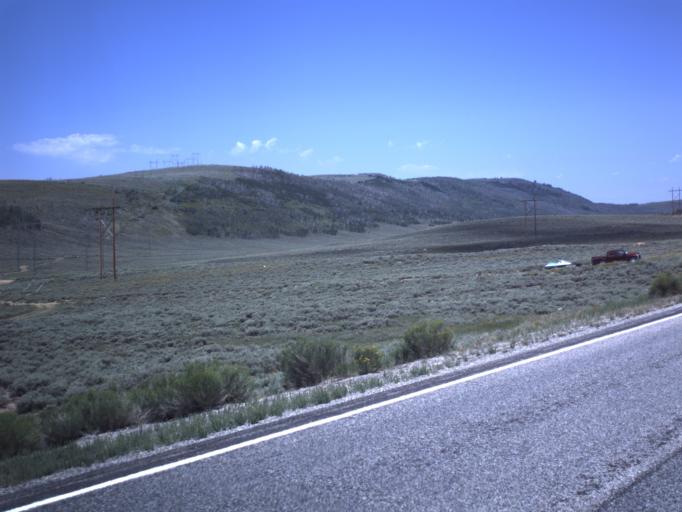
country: US
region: Utah
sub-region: Carbon County
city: Helper
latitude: 39.8386
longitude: -111.1293
